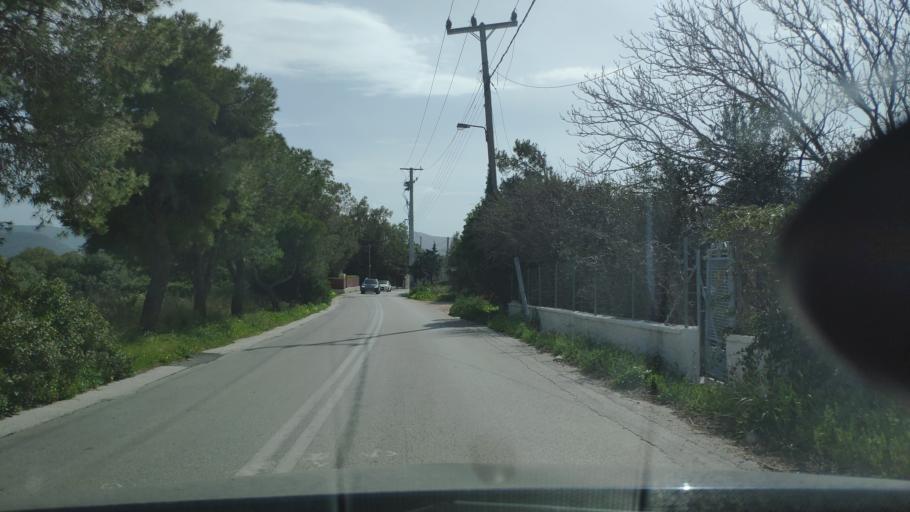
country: GR
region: Attica
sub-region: Nomarchia Anatolikis Attikis
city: Limin Mesoyaias
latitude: 37.8975
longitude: 24.0238
